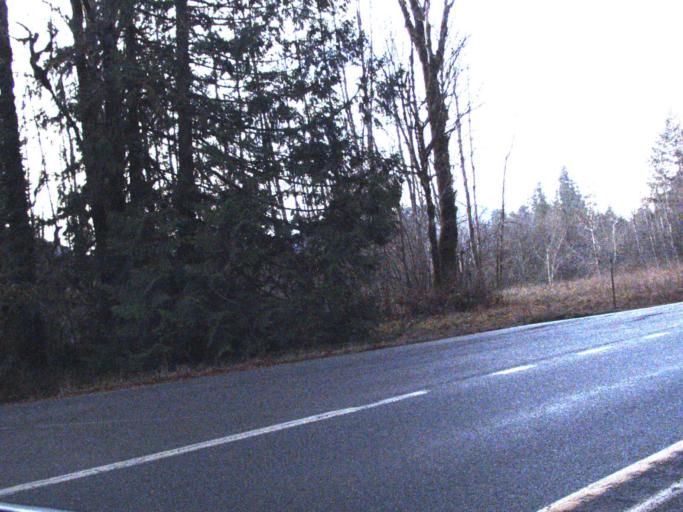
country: US
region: Washington
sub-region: Snohomish County
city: Darrington
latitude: 48.4874
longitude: -121.5965
